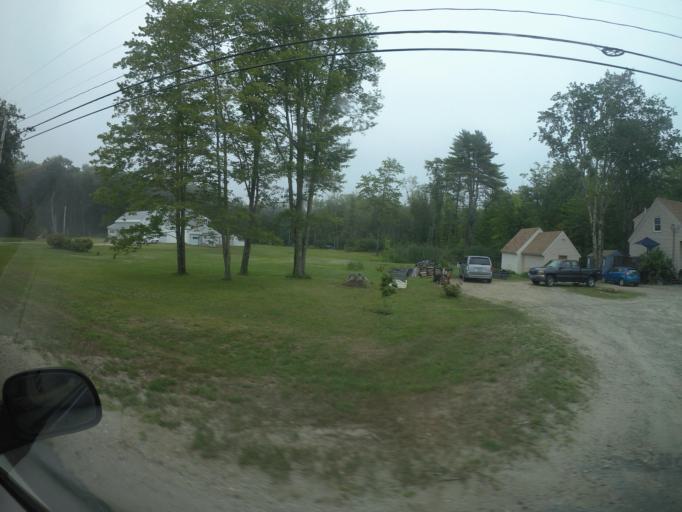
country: US
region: Maine
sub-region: York County
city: Arundel
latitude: 43.4033
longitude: -70.4877
